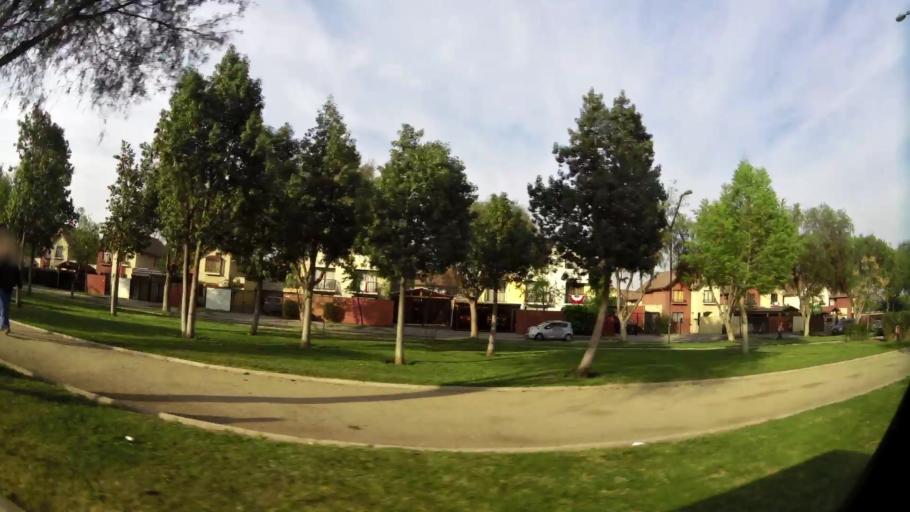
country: CL
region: Santiago Metropolitan
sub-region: Provincia de Maipo
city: San Bernardo
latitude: -33.5597
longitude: -70.7827
